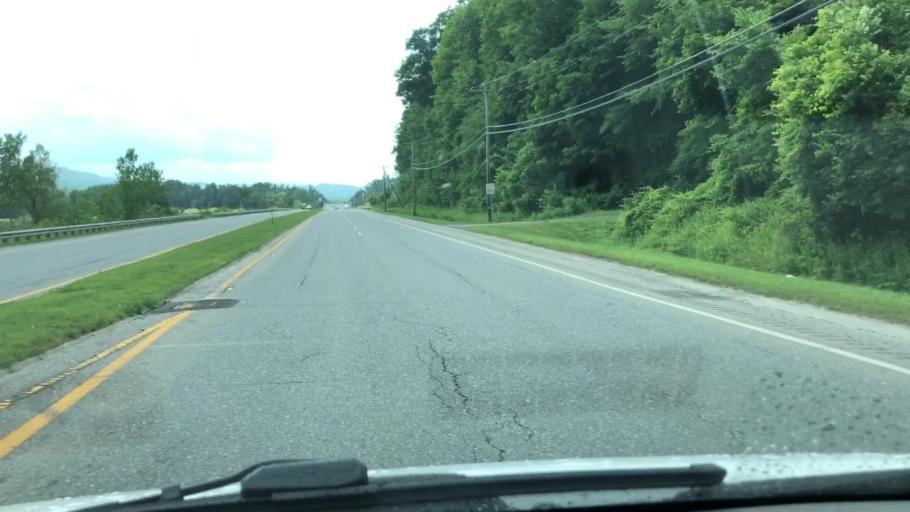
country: US
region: Massachusetts
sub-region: Berkshire County
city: North Adams
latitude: 42.6754
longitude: -73.1074
